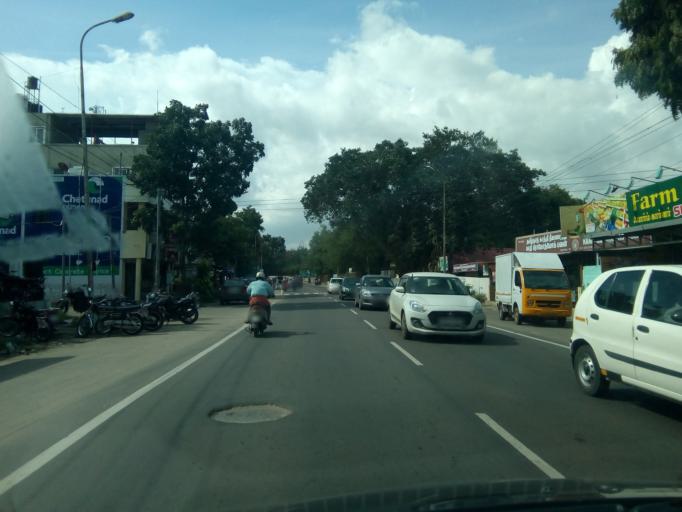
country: IN
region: Tamil Nadu
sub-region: Coimbatore
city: Singanallur
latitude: 11.0154
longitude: 77.0236
